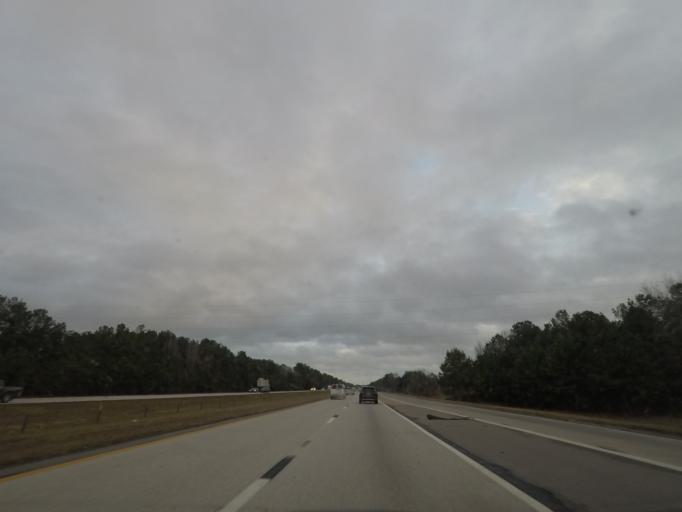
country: US
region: South Carolina
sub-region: Dorchester County
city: Saint George
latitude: 33.2737
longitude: -80.5678
